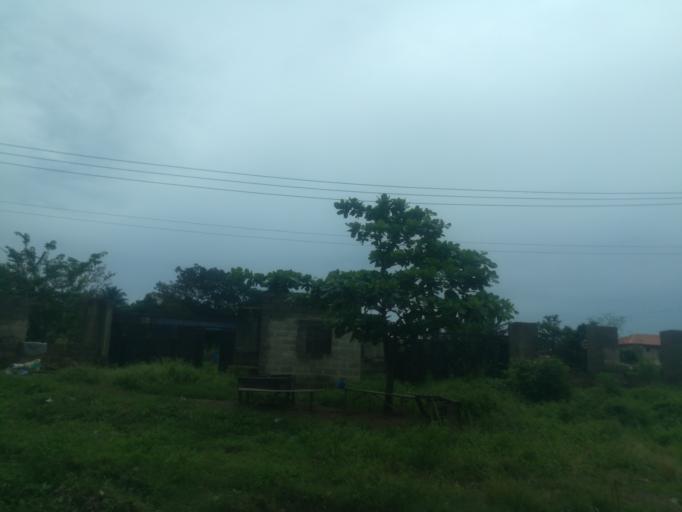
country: NG
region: Oyo
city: Ibadan
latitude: 7.3368
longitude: 3.8934
